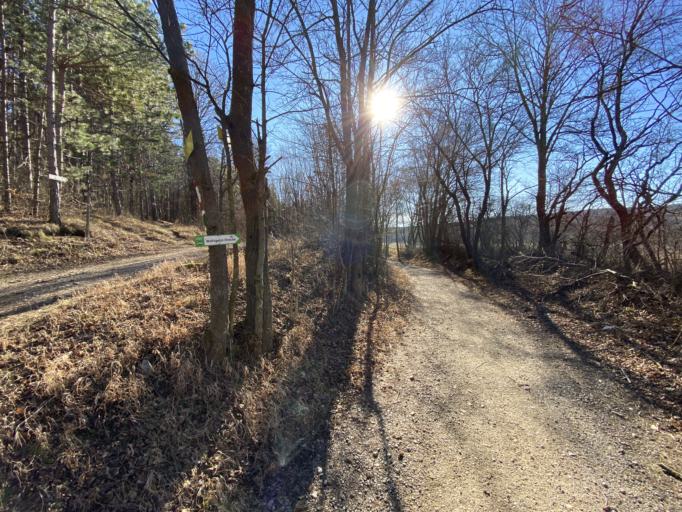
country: AT
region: Lower Austria
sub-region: Politischer Bezirk Baden
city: Berndorf
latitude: 47.9749
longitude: 16.1446
